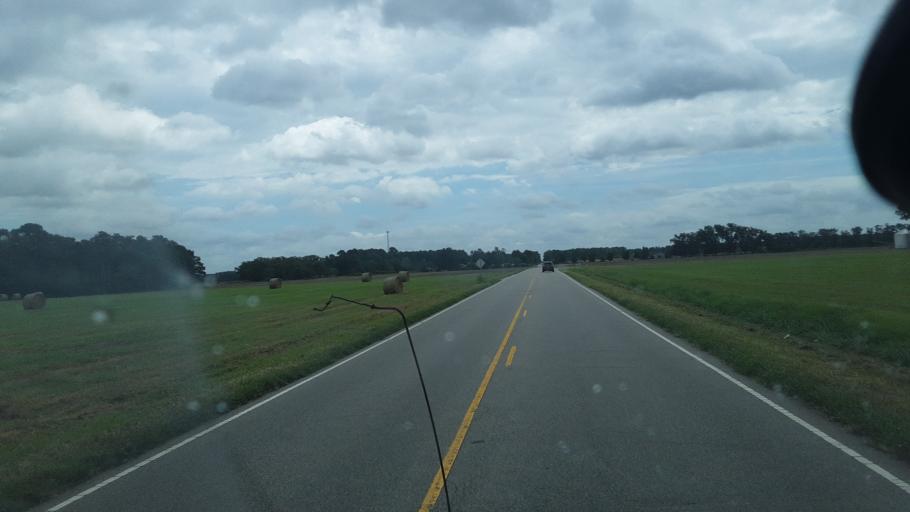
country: US
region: North Carolina
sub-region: Scotland County
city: Laurinburg
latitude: 34.6840
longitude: -79.4318
